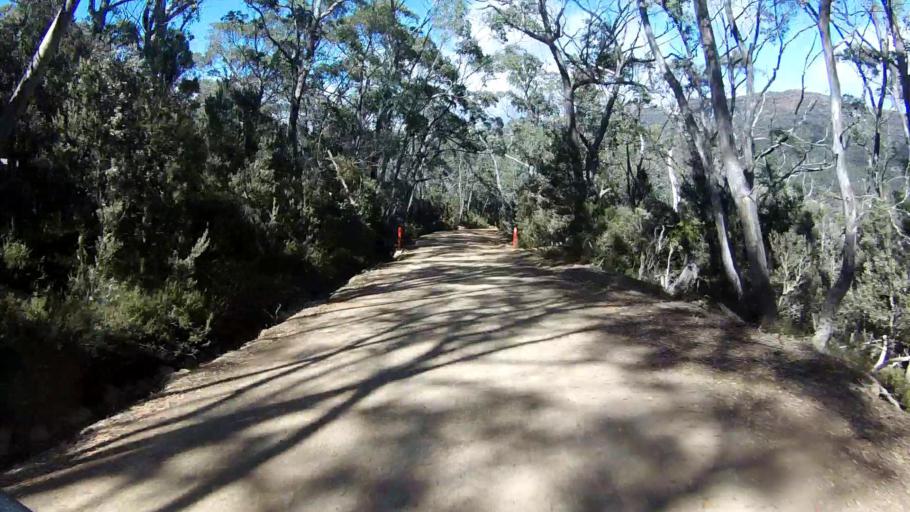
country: AU
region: Tasmania
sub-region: Derwent Valley
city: New Norfolk
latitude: -42.6845
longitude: 146.6061
